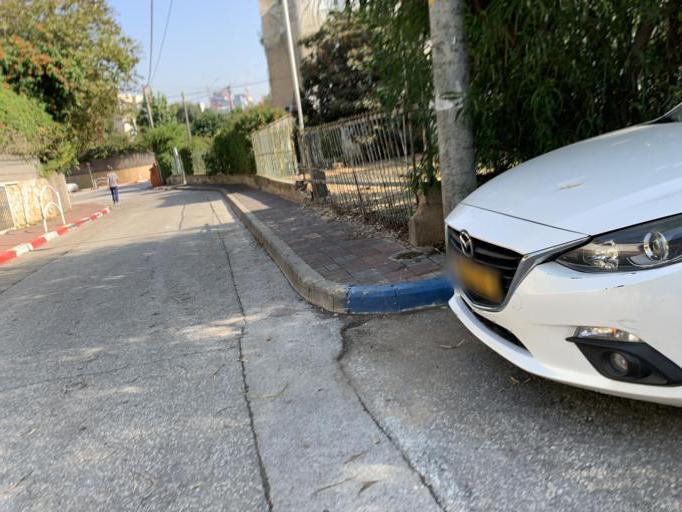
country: IL
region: Tel Aviv
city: Ramat Gan
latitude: 32.0907
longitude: 34.8103
